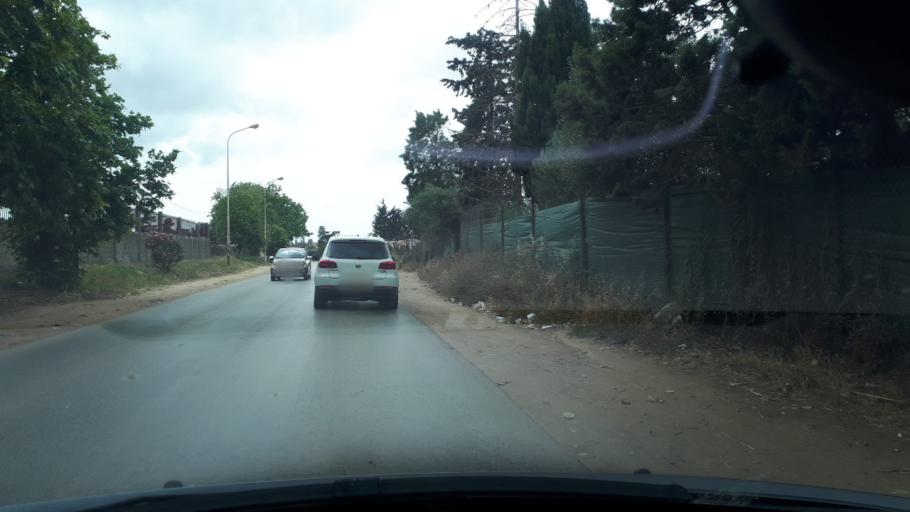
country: DZ
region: Tipaza
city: Cheraga
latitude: 36.7425
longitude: 2.9054
